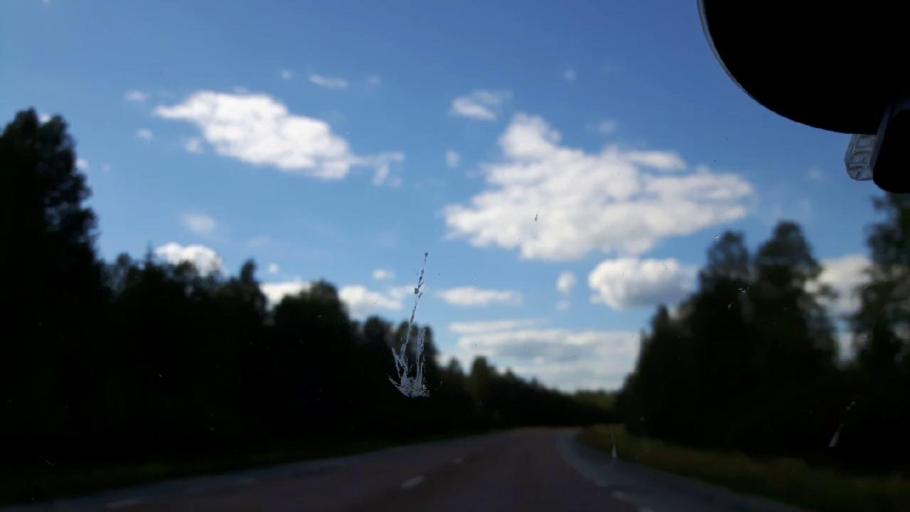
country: SE
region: Jaemtland
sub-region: Braecke Kommun
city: Braecke
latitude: 62.8190
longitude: 15.3353
